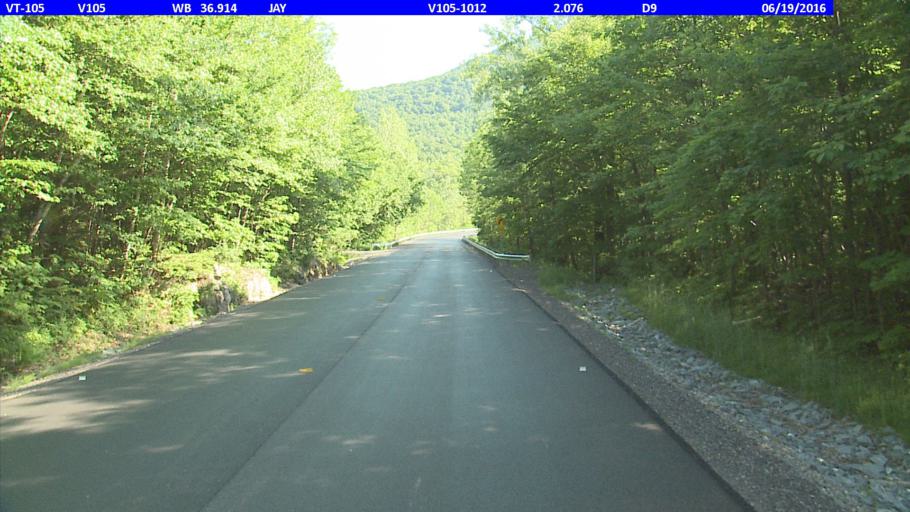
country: US
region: Vermont
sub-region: Franklin County
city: Richford
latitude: 44.9729
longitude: -72.5215
